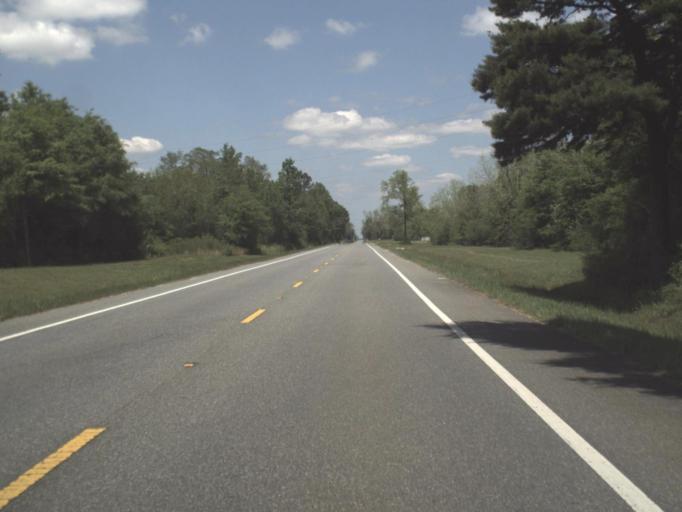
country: US
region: Florida
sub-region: Santa Rosa County
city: Point Baker
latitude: 30.7494
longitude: -87.0425
